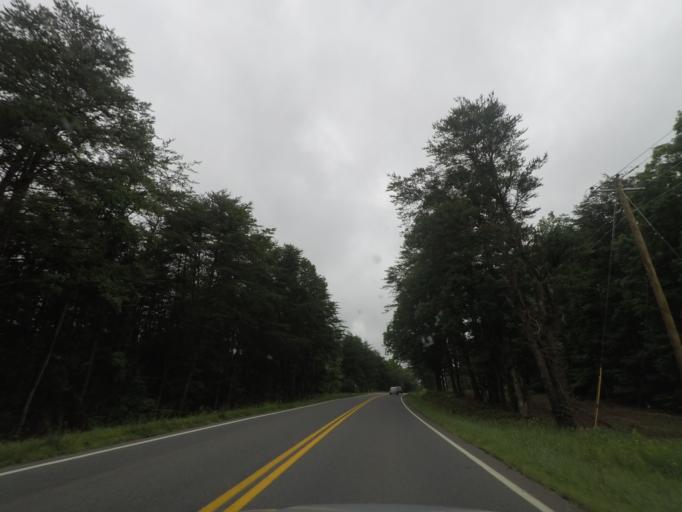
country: US
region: Virginia
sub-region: Fluvanna County
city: Palmyra
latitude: 37.8942
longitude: -78.2608
